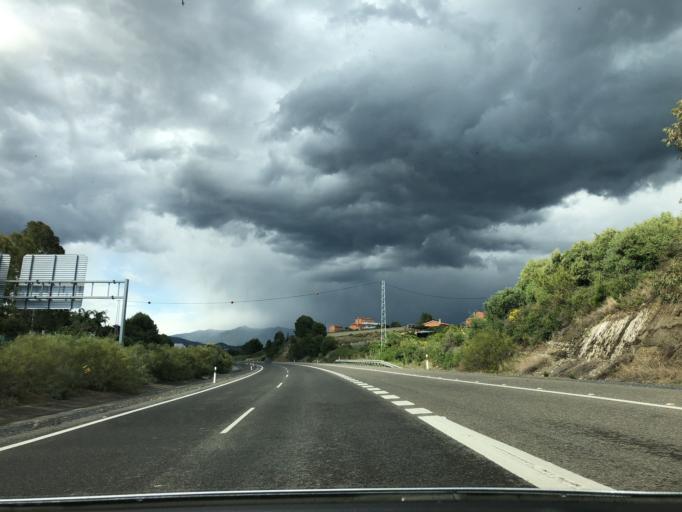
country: ES
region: Andalusia
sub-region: Provincia de Malaga
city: Estepona
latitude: 36.4394
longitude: -5.1333
